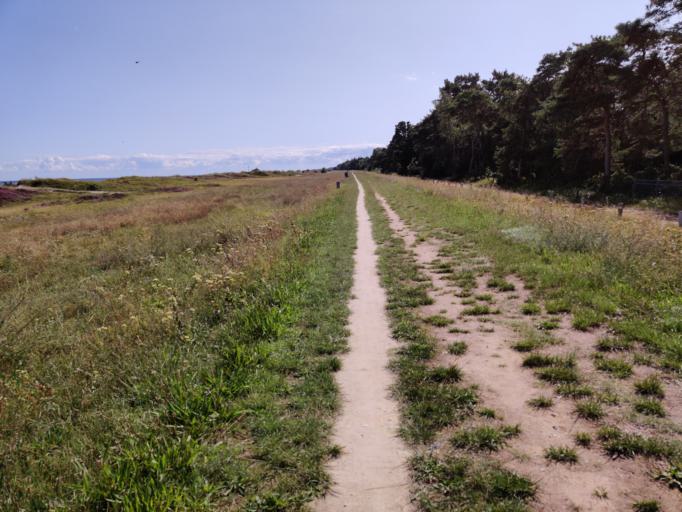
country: DK
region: Zealand
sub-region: Guldborgsund Kommune
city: Nykobing Falster
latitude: 54.6533
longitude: 11.9597
